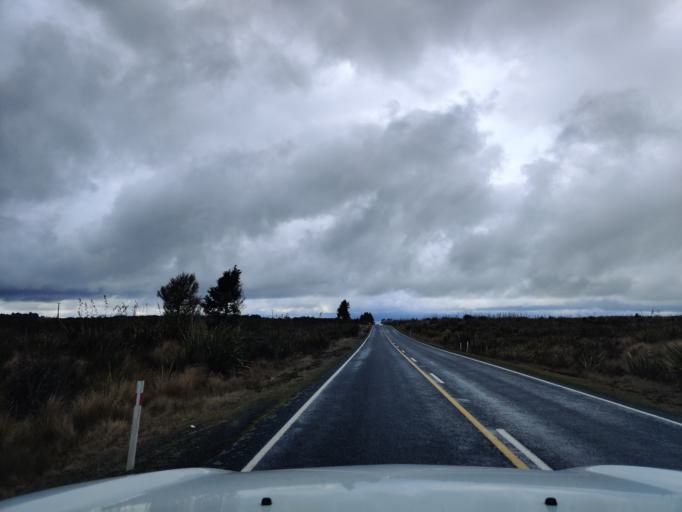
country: NZ
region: Manawatu-Wanganui
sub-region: Ruapehu District
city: Waiouru
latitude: -39.1893
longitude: 175.4017
